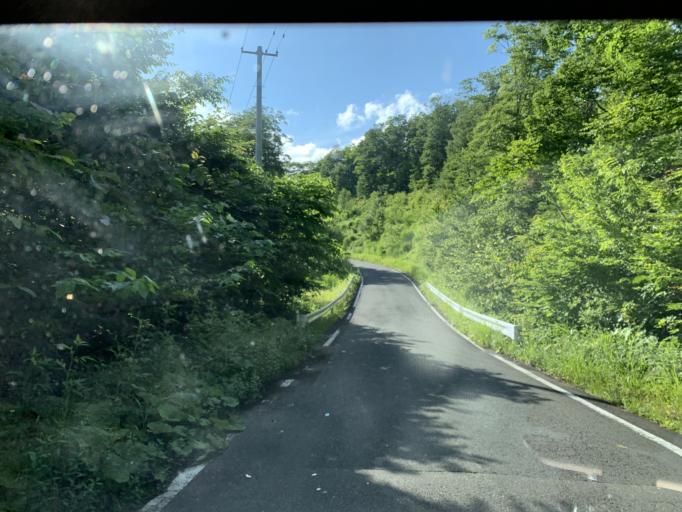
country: JP
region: Iwate
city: Ichinoseki
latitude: 38.9059
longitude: 140.8509
